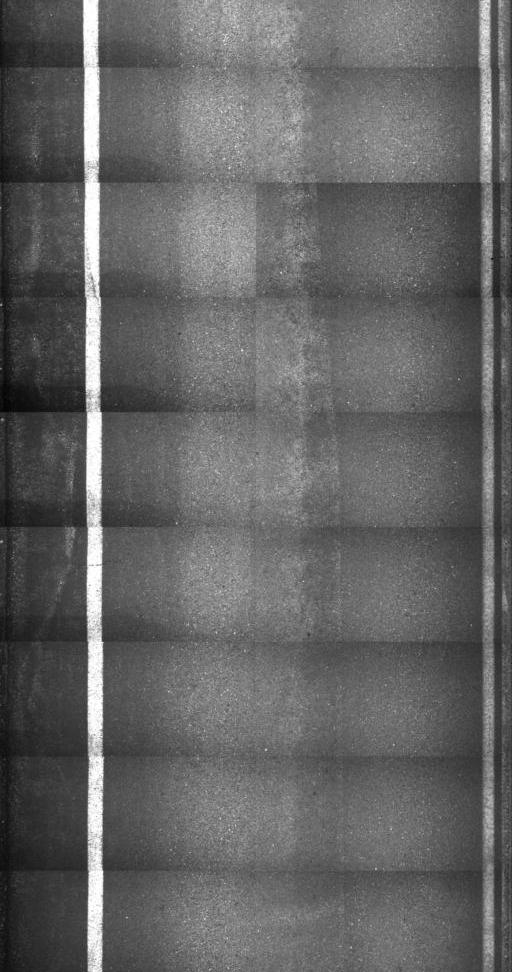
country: US
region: Vermont
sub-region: Caledonia County
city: Lyndonville
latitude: 44.6633
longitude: -72.1617
